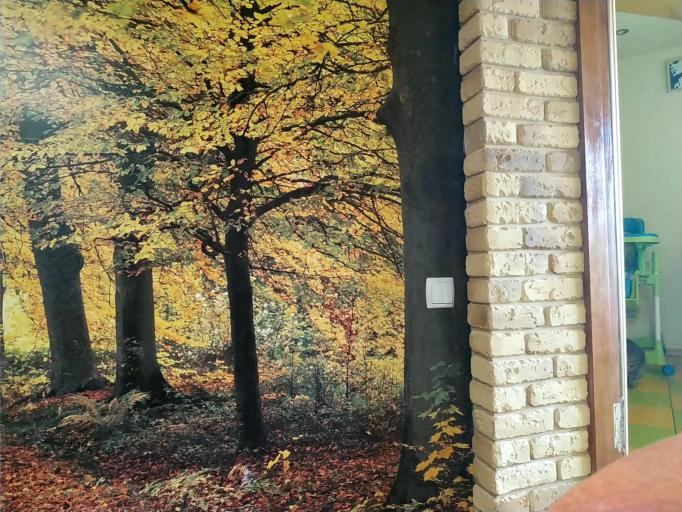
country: RU
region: Smolensk
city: Ozernyy
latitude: 55.4725
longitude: 32.6530
